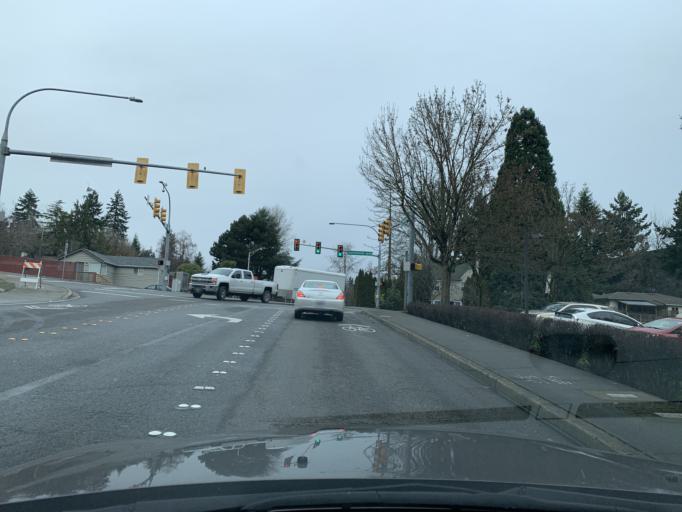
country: US
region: Washington
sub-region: King County
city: SeaTac
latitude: 47.4656
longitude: -122.2811
